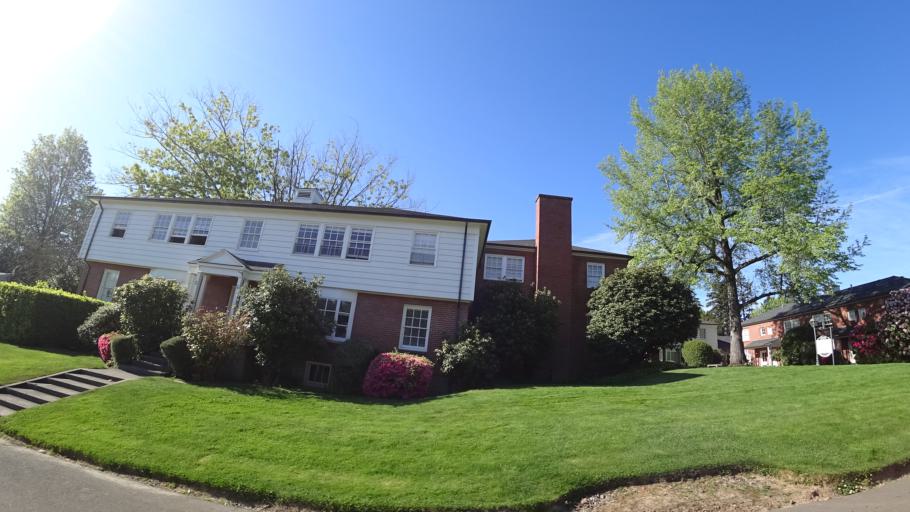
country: US
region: Oregon
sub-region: Washington County
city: Raleigh Hills
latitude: 45.4900
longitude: -122.7592
